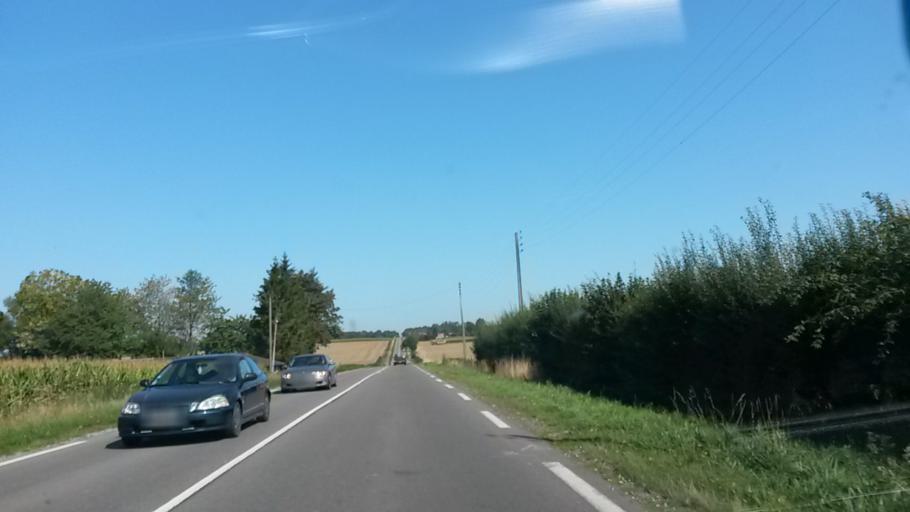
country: FR
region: Nord-Pas-de-Calais
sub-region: Departement du Nord
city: Avesnelles
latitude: 50.1797
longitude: 3.9525
